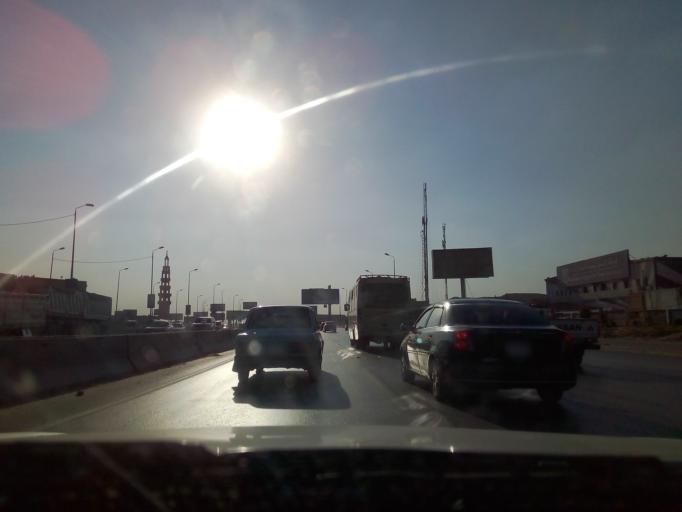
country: EG
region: Muhafazat al Qahirah
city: Cairo
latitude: 29.9916
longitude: 31.2935
